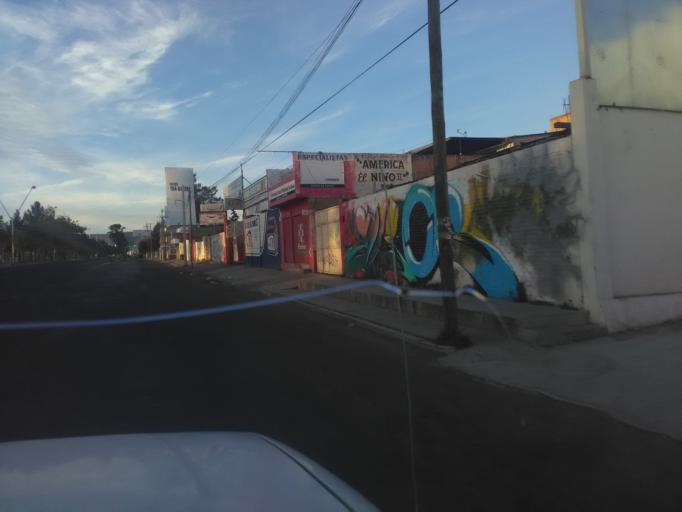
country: MX
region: Durango
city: Victoria de Durango
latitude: 23.9915
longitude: -104.6637
